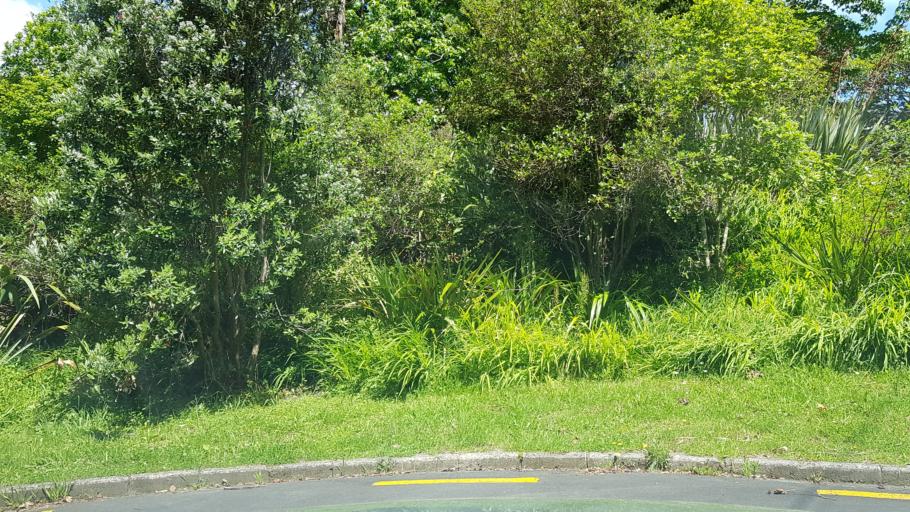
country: NZ
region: Auckland
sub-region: Auckland
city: North Shore
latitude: -36.8153
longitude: 174.7337
